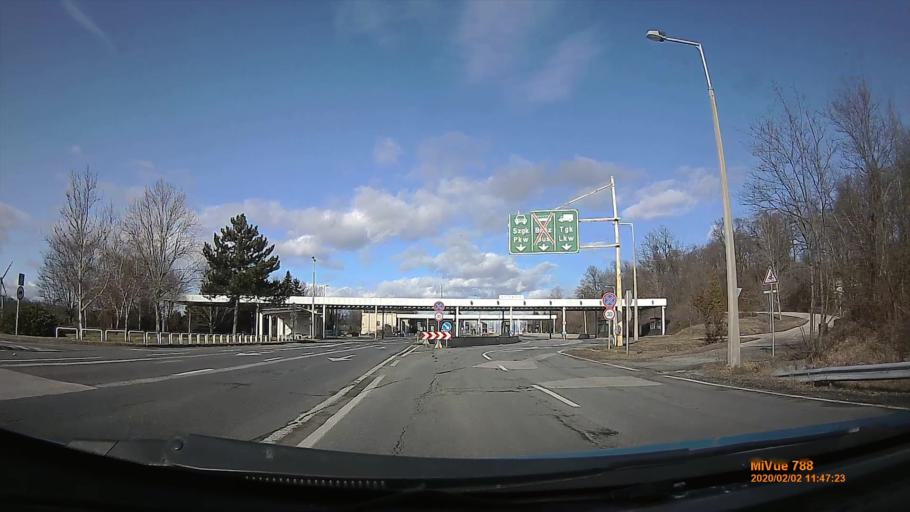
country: AT
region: Burgenland
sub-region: Eisenstadt-Umgebung
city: Klingenbach
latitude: 47.7393
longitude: 16.5470
